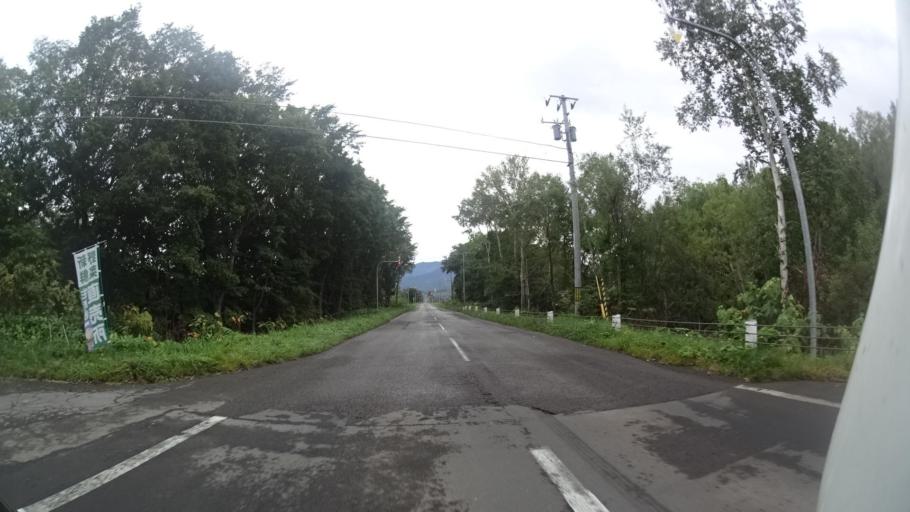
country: JP
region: Hokkaido
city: Shibetsu
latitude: 43.8733
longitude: 144.7221
